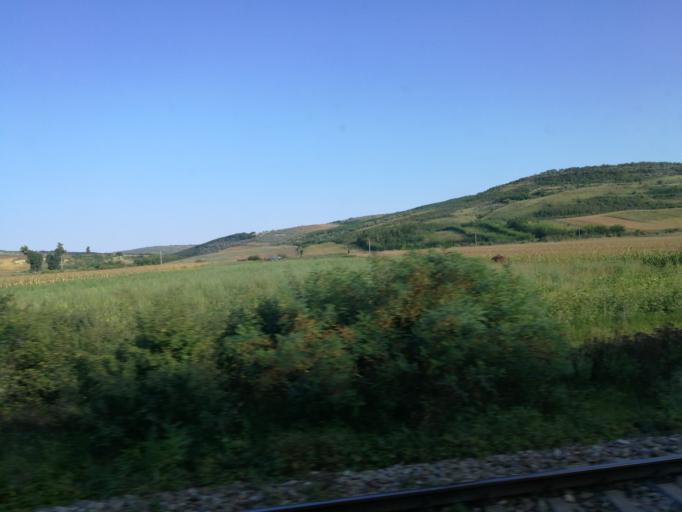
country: RO
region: Vaslui
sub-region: Comuna Banca
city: Banca
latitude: 46.3469
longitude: 27.7998
